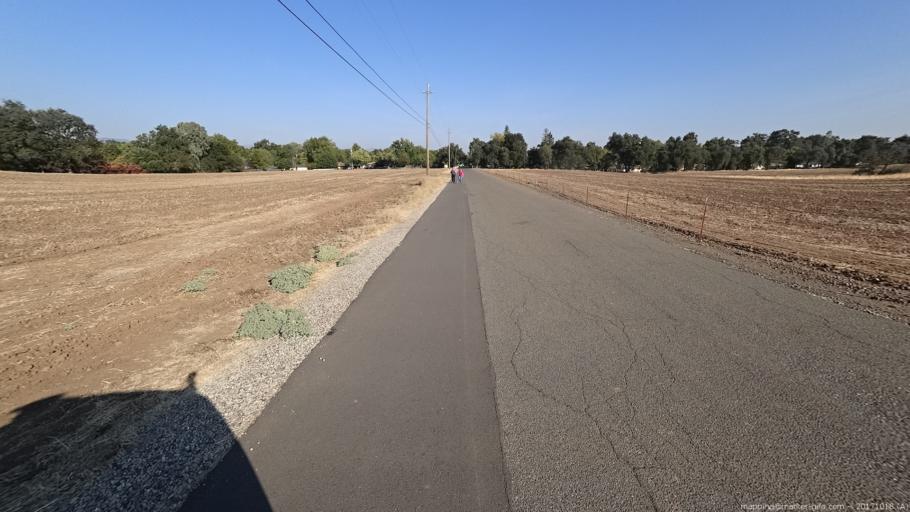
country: US
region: California
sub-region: Shasta County
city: Redding
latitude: 40.5596
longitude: -122.3700
